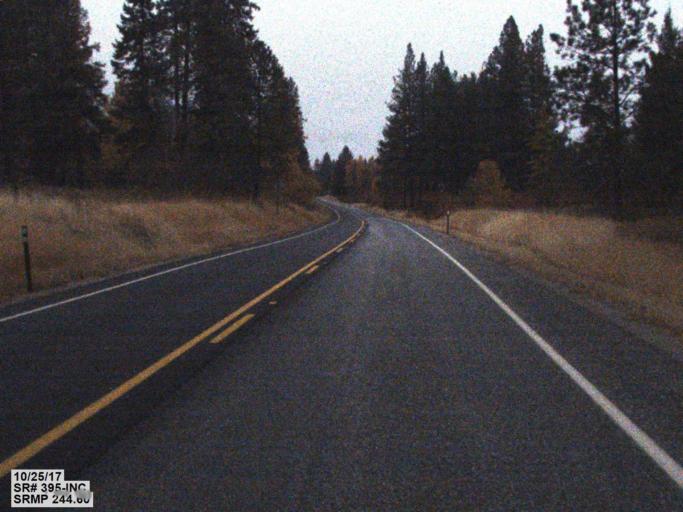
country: US
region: Washington
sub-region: Stevens County
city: Kettle Falls
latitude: 48.6646
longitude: -118.1142
